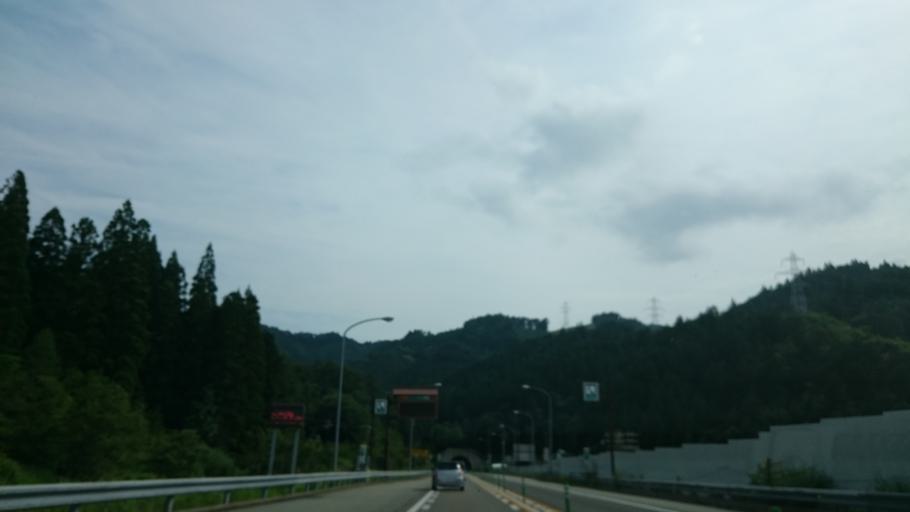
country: JP
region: Gifu
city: Gujo
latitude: 35.9220
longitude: 136.8719
